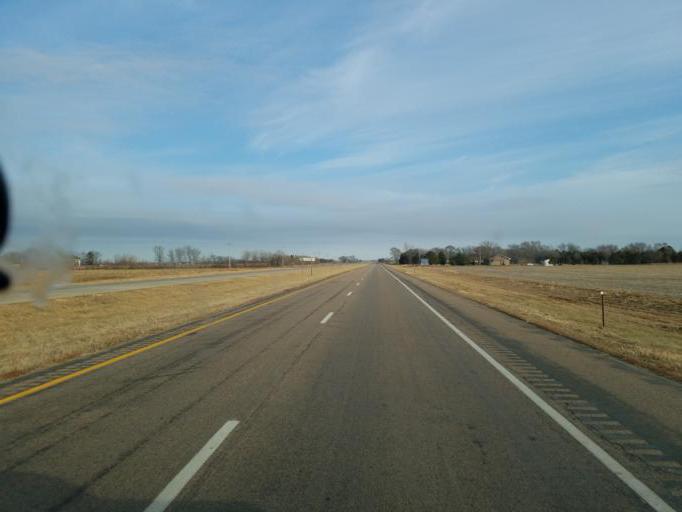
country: US
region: South Dakota
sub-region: Union County
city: Dakota Dunes
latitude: 42.4483
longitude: -96.5352
